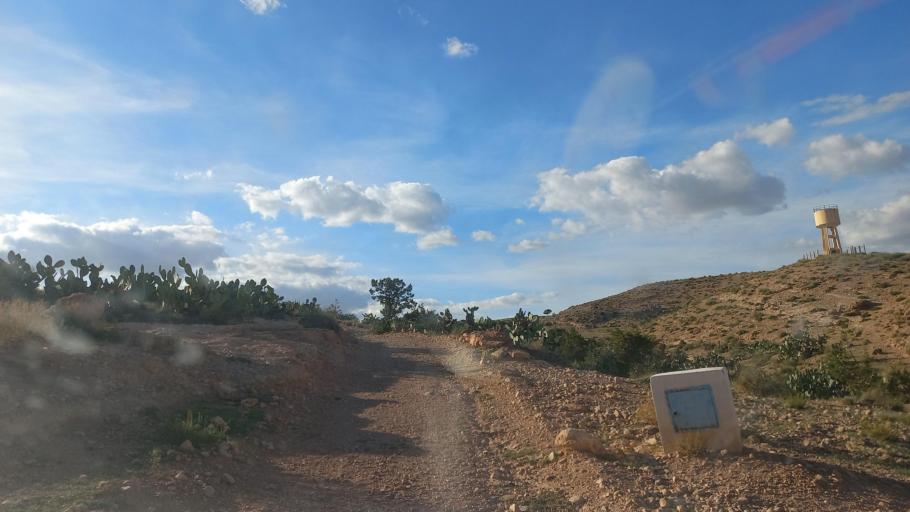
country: TN
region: Al Qasrayn
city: Sbiba
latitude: 35.3822
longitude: 9.0201
